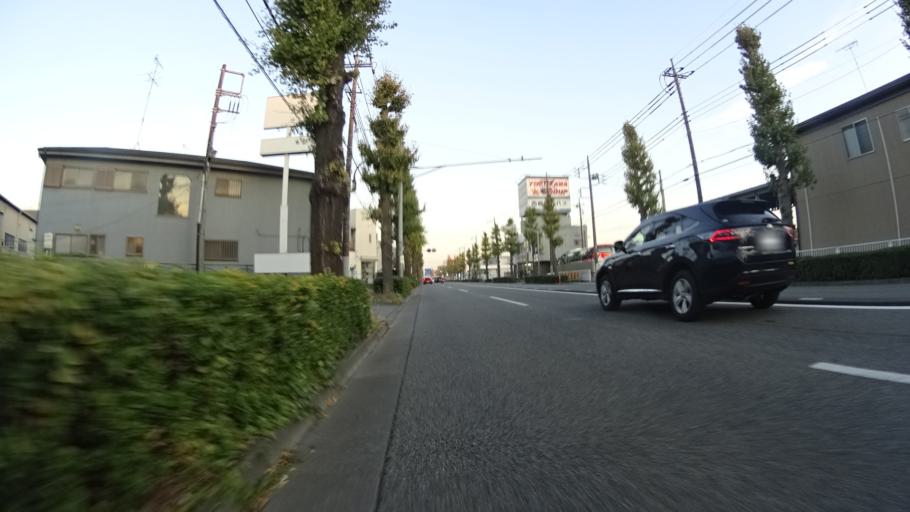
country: JP
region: Tokyo
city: Hino
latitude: 35.6985
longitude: 139.3702
